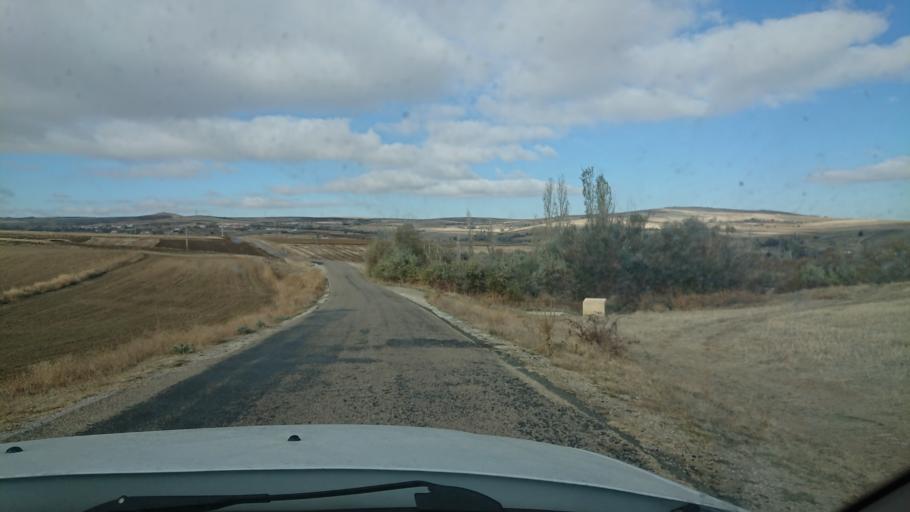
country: TR
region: Aksaray
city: Agacoren
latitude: 38.8187
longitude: 33.9783
